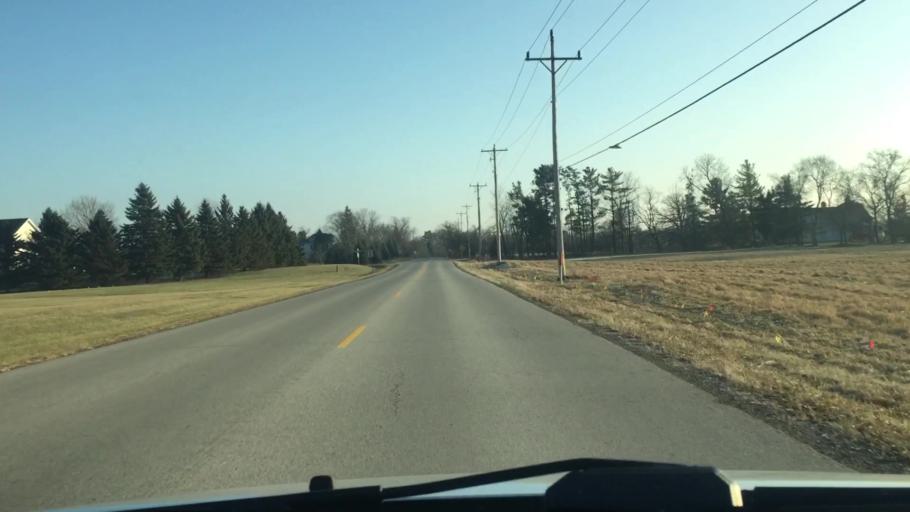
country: US
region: Wisconsin
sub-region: Waukesha County
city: Dousman
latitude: 43.0362
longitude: -88.4825
